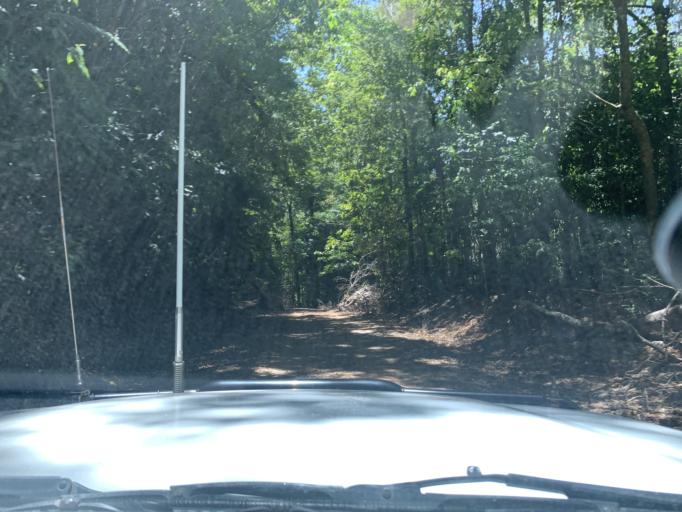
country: AU
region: Queensland
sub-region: Cairns
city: Redlynch
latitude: -16.9625
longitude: 145.6461
